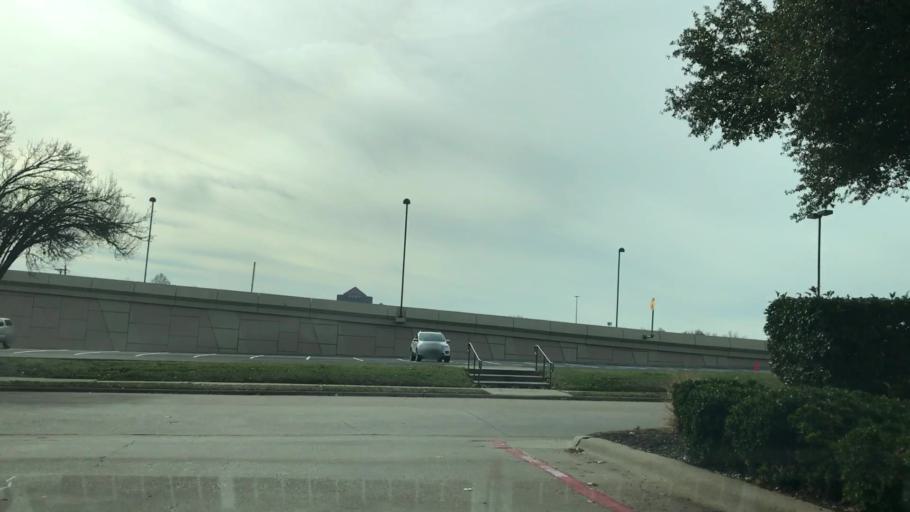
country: US
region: Texas
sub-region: Collin County
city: Plano
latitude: 32.9841
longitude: -96.7137
